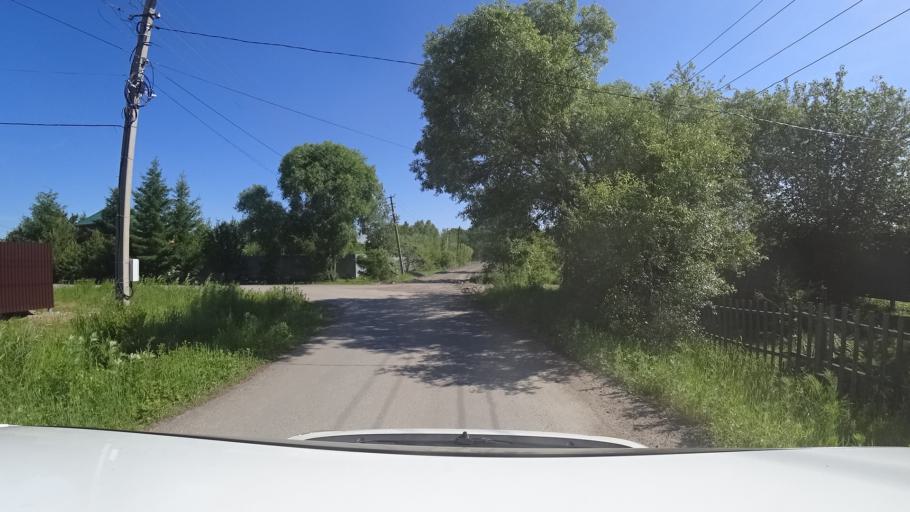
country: RU
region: Khabarovsk Krai
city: Topolevo
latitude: 48.5505
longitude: 135.1691
